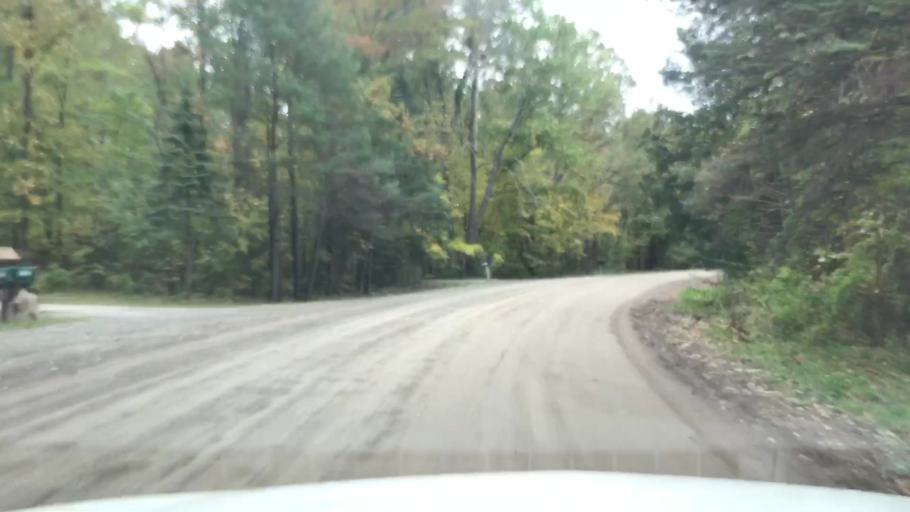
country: US
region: Michigan
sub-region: Oakland County
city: Rochester
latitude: 42.7455
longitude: -83.0993
